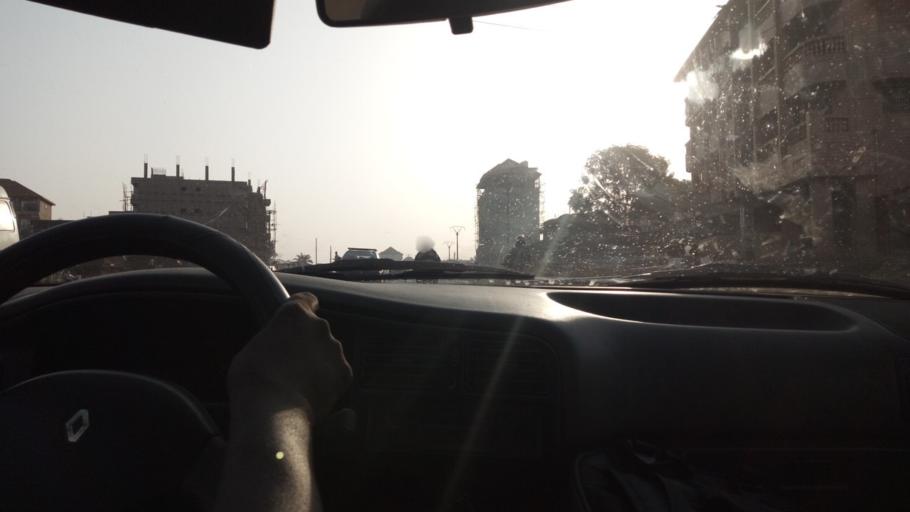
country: GN
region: Kindia
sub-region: Prefecture de Dubreka
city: Dubreka
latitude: 9.6735
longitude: -13.5490
